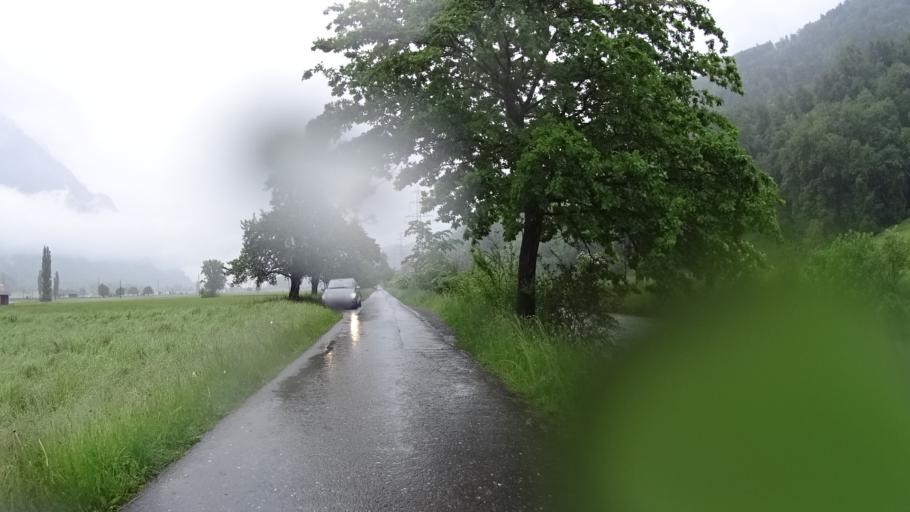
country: CH
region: Saint Gallen
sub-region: Wahlkreis Sarganserland
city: Flums
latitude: 47.0793
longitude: 9.3655
